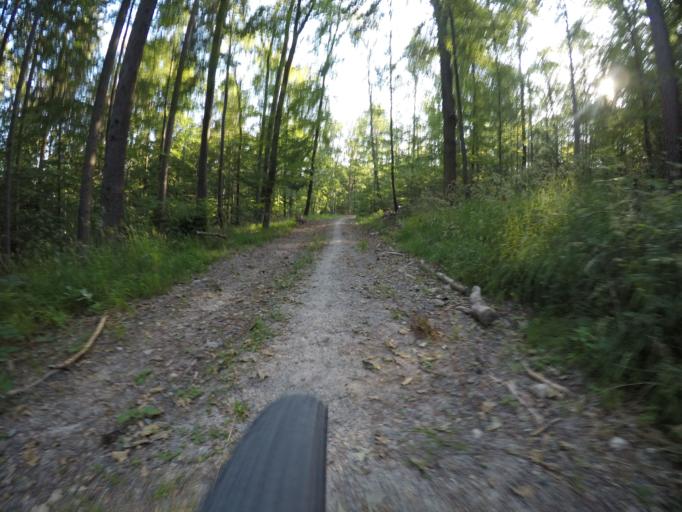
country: DE
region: Baden-Wuerttemberg
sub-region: Regierungsbezirk Stuttgart
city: Gerlingen
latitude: 48.7517
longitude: 9.0932
